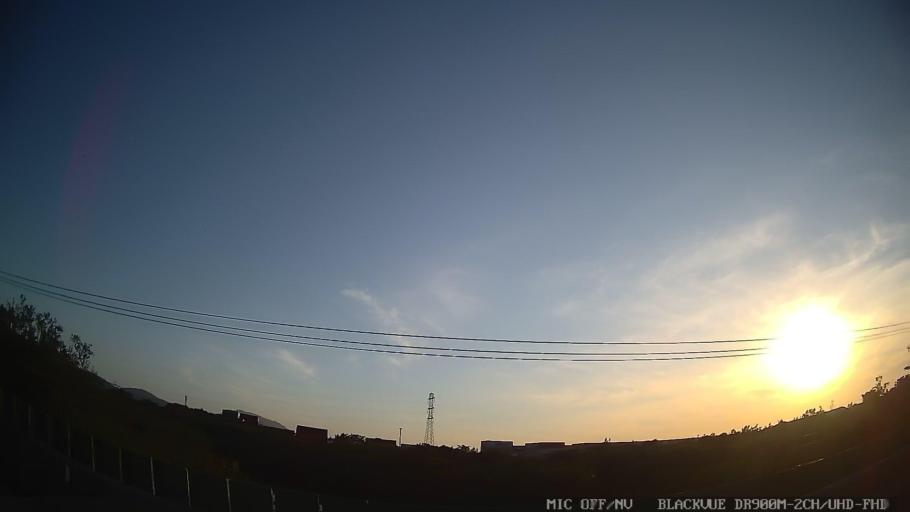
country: BR
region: Sao Paulo
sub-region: Guaruja
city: Guaruja
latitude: -23.9803
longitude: -46.2665
